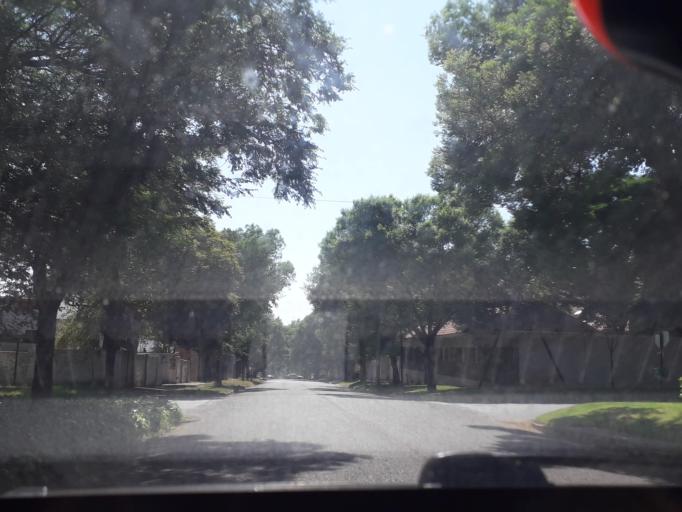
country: ZA
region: Gauteng
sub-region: City of Johannesburg Metropolitan Municipality
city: Johannesburg
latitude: -26.1485
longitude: 28.0660
